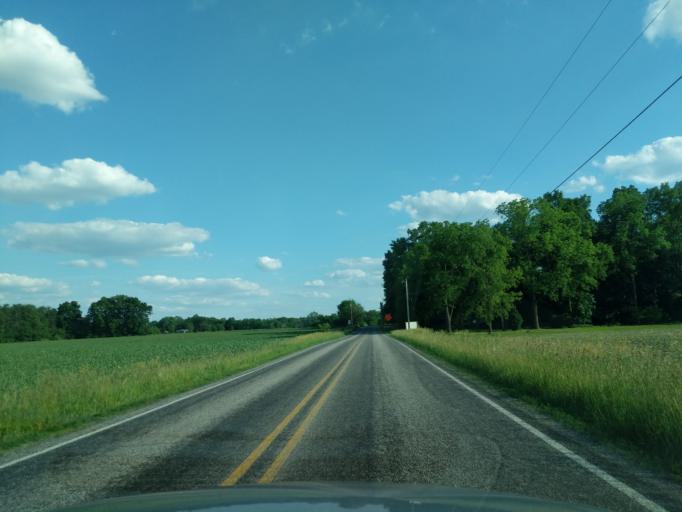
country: US
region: Indiana
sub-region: Kosciusko County
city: North Webster
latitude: 41.3048
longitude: -85.6435
